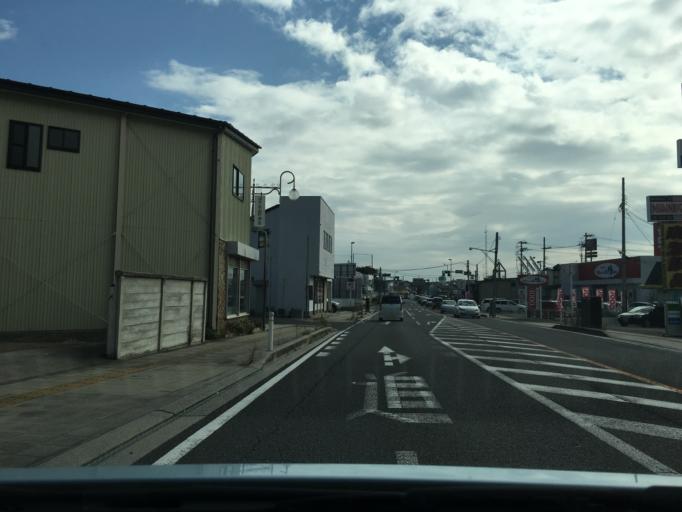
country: JP
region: Fukushima
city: Koriyama
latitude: 37.3847
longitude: 140.3594
